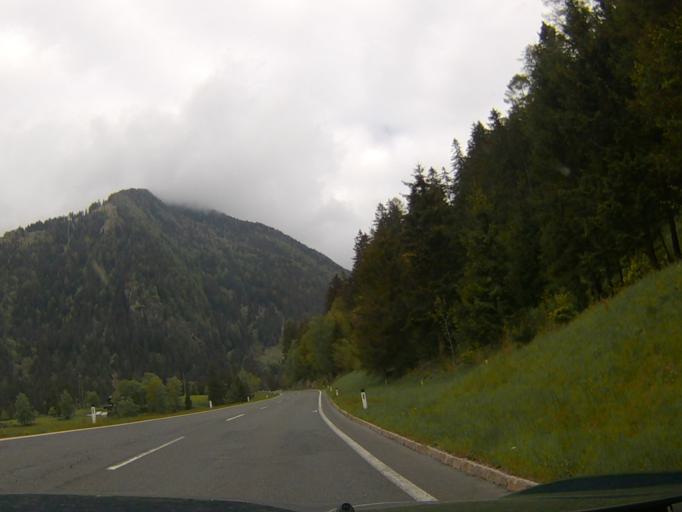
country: AT
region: Carinthia
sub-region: Politischer Bezirk Spittal an der Drau
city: Obervellach
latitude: 46.9444
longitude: 13.1855
